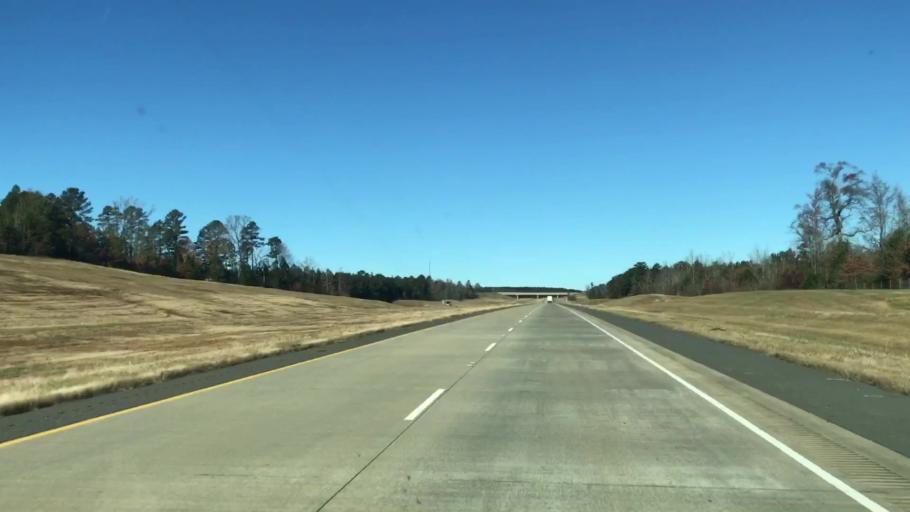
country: US
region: Louisiana
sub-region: Caddo Parish
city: Vivian
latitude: 32.9145
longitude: -93.8758
